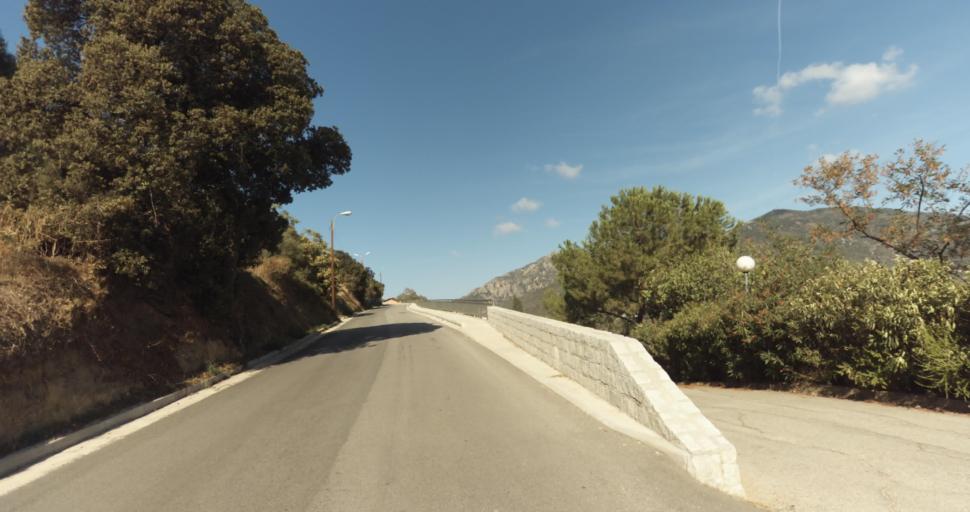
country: FR
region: Corsica
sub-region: Departement de la Corse-du-Sud
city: Ajaccio
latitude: 41.9251
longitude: 8.7261
